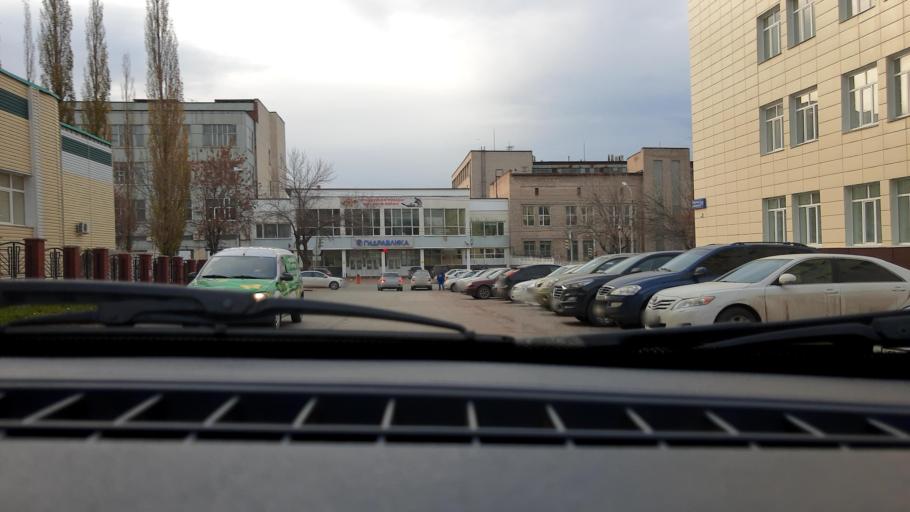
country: RU
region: Bashkortostan
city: Ufa
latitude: 54.7448
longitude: 55.9817
